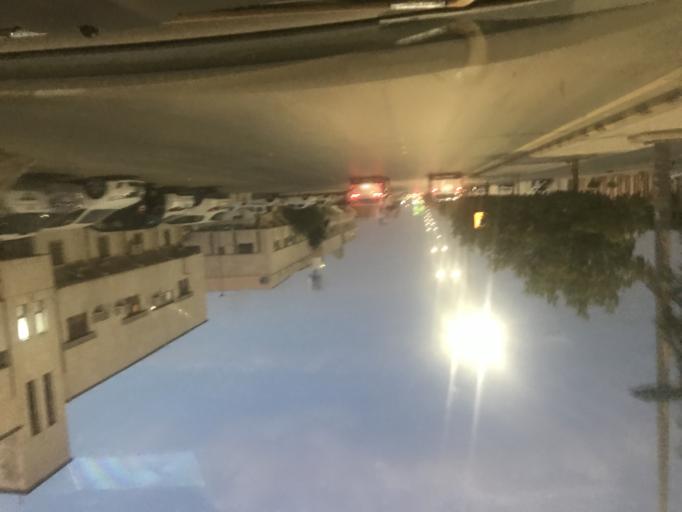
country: SA
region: Ar Riyad
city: Riyadh
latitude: 24.7347
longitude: 46.7595
